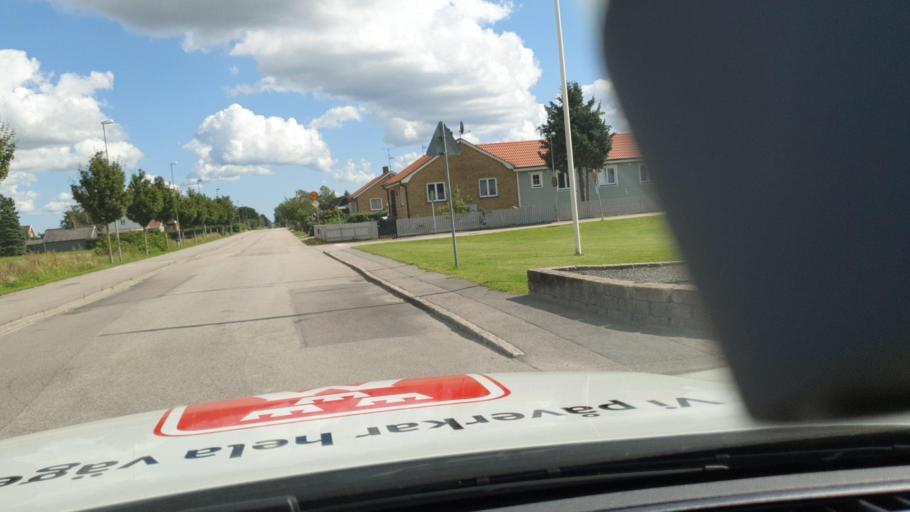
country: SE
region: Skane
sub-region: Astorps Kommun
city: Kvidinge
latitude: 56.1324
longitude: 13.0586
